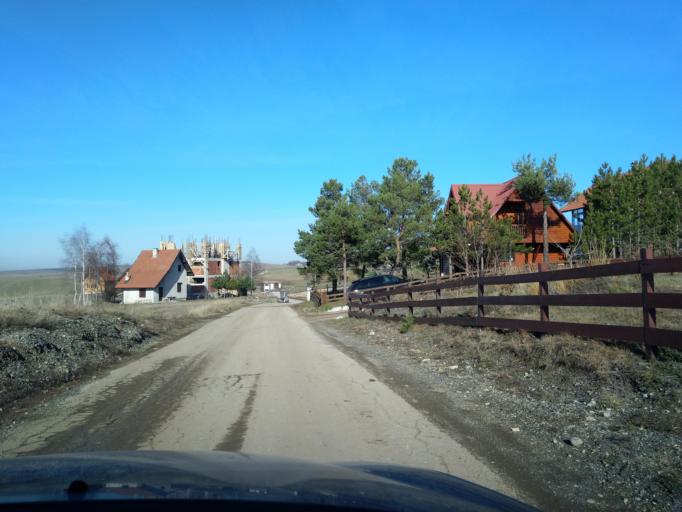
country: RS
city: Zlatibor
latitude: 43.7425
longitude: 19.6772
